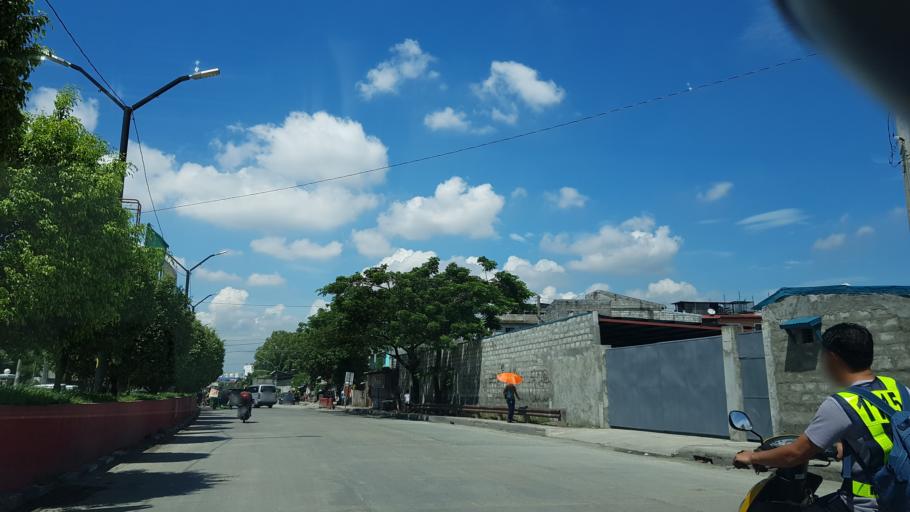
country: PH
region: Calabarzon
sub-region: Province of Rizal
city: Pateros
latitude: 14.5336
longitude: 121.0733
